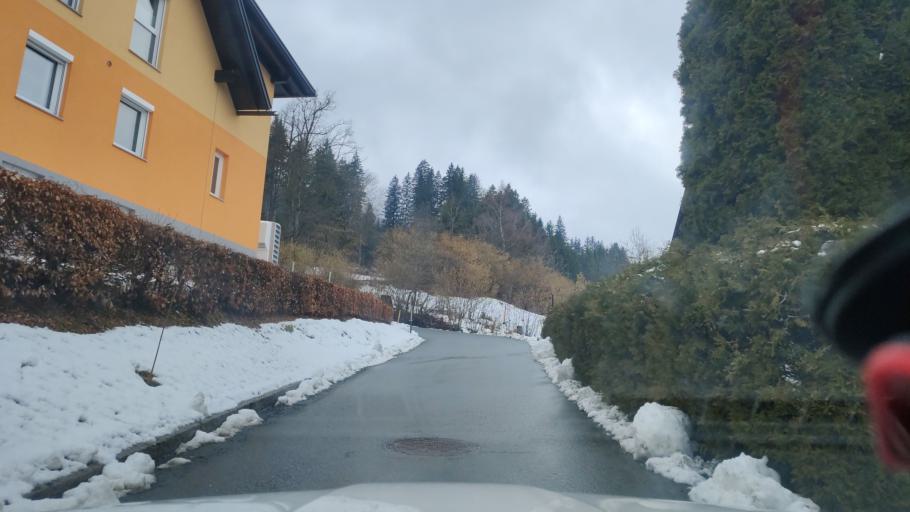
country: AT
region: Carinthia
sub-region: Politischer Bezirk Hermagor
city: Hermagor
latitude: 46.6280
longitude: 13.3561
